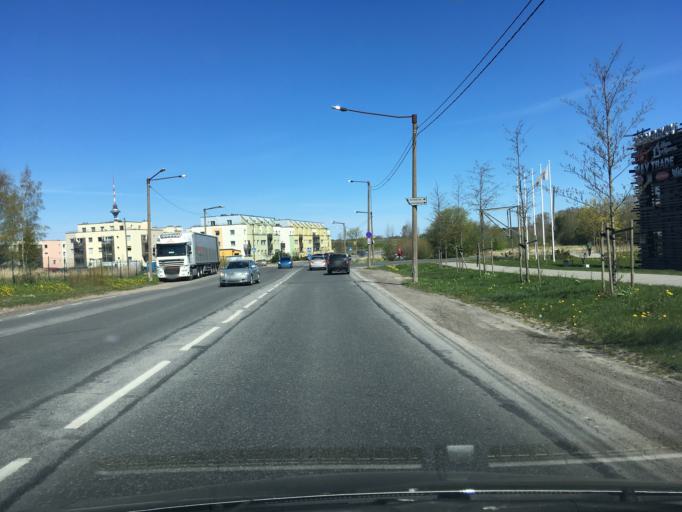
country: EE
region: Harju
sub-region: Tallinna linn
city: Kose
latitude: 59.4513
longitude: 24.8915
